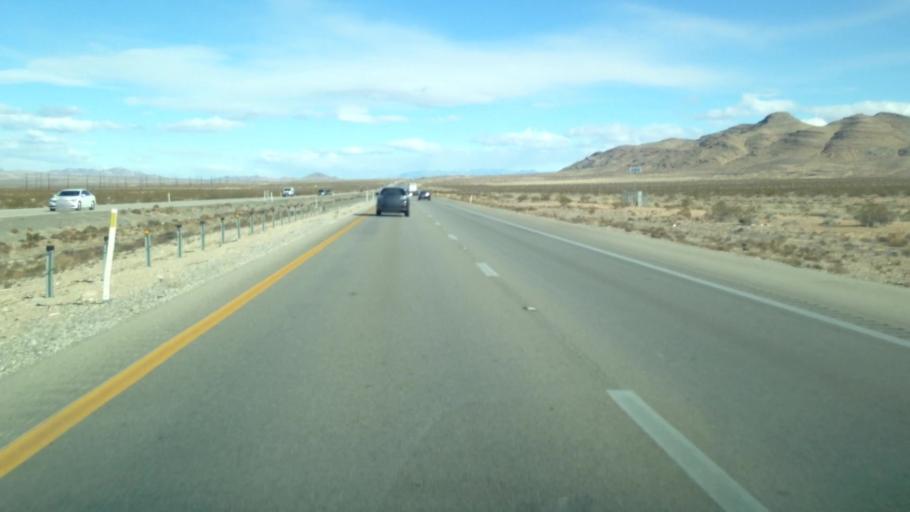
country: US
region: Nevada
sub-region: Clark County
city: Nellis Air Force Base
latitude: 36.4203
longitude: -114.8655
